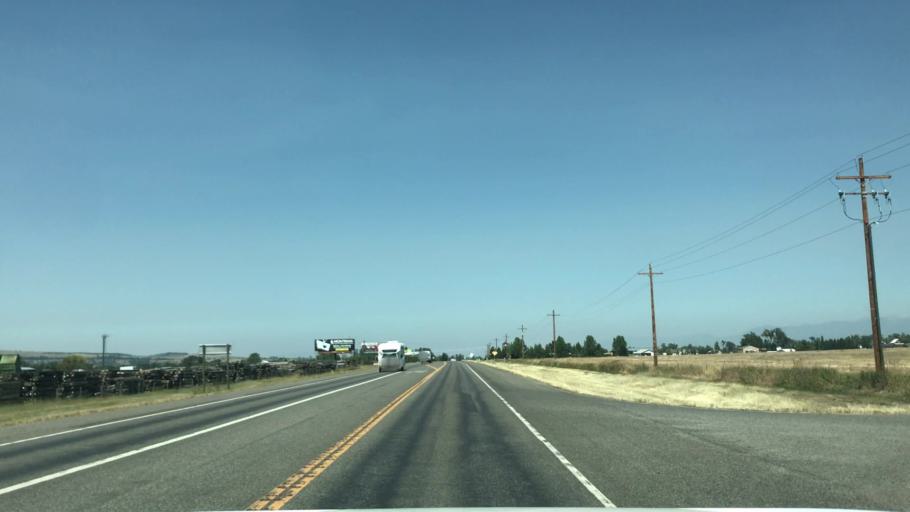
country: US
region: Montana
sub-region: Gallatin County
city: Four Corners
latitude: 45.5845
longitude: -111.1970
